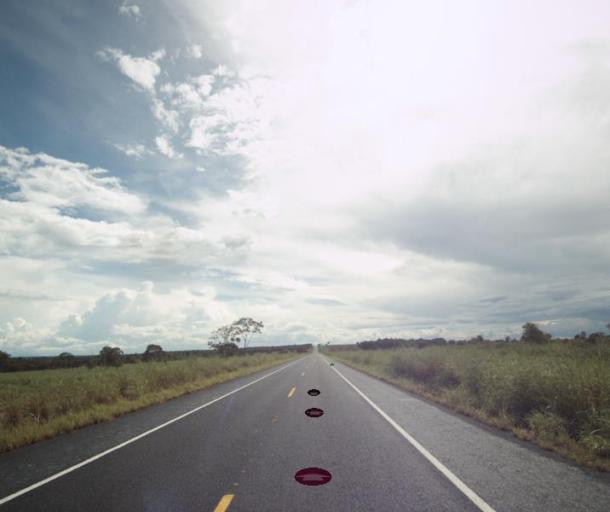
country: BR
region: Goias
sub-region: Sao Miguel Do Araguaia
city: Sao Miguel do Araguaia
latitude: -13.2938
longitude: -50.3822
